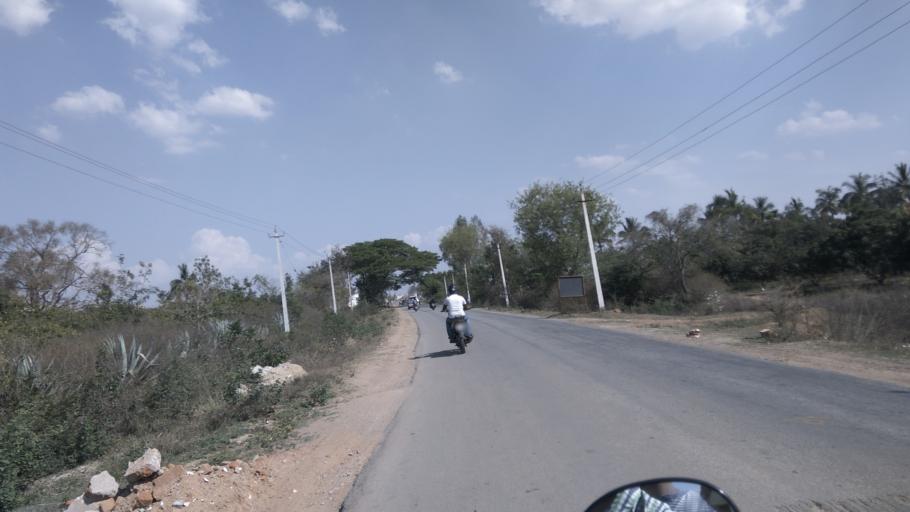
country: IN
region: Karnataka
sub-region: Kolar
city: Mulbagal
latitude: 13.1689
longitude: 78.3616
